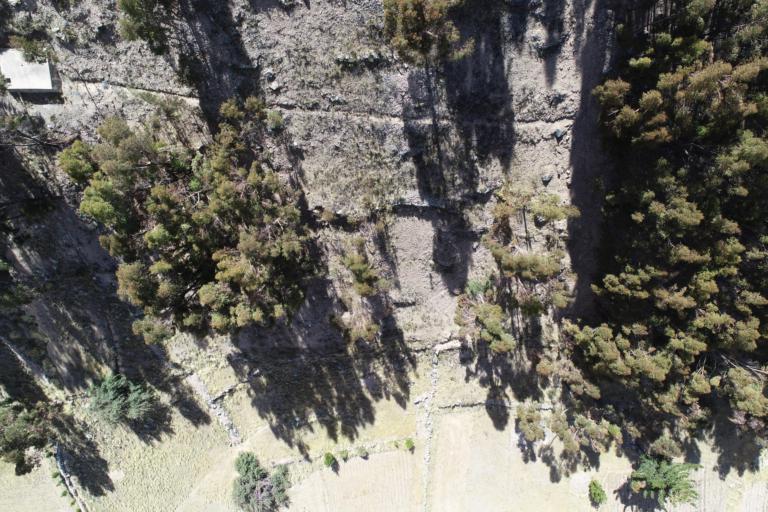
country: BO
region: La Paz
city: Achacachi
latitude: -15.8935
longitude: -68.9069
